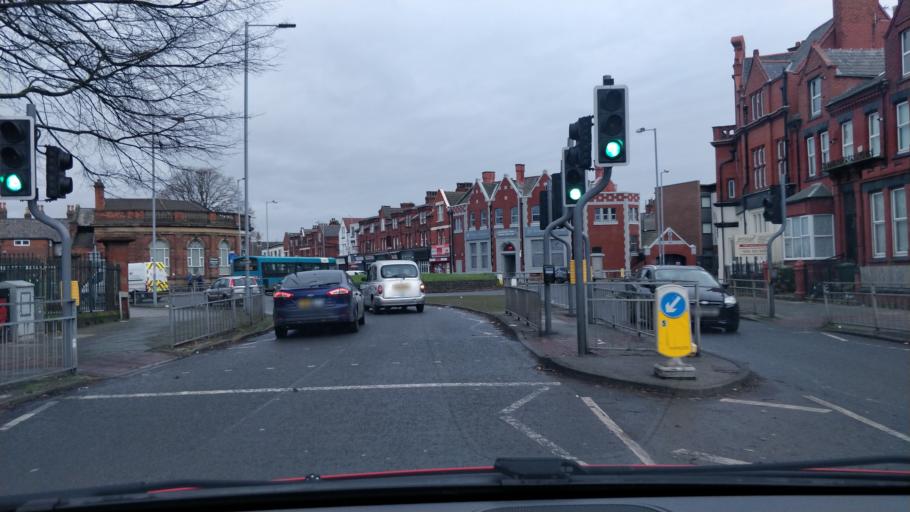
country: GB
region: England
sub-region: Sefton
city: Litherland
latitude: 53.4581
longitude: -2.9923
